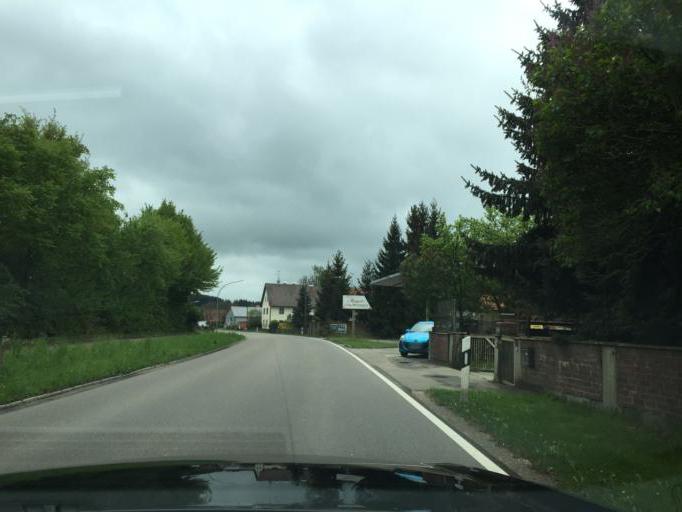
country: DE
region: Bavaria
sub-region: Swabia
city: Buttenwiesen
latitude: 48.5978
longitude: 10.7195
